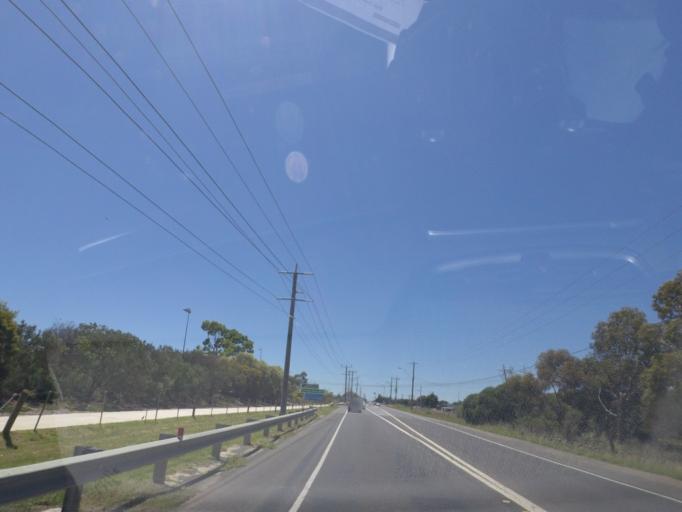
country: AU
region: Victoria
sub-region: Whittlesea
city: Epping
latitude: -37.6248
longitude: 145.0285
